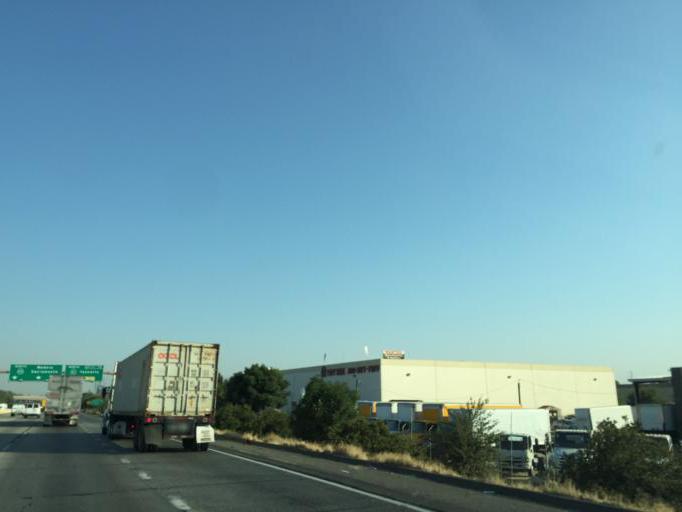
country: US
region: California
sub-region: Fresno County
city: Fresno
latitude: 36.7103
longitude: -119.7772
